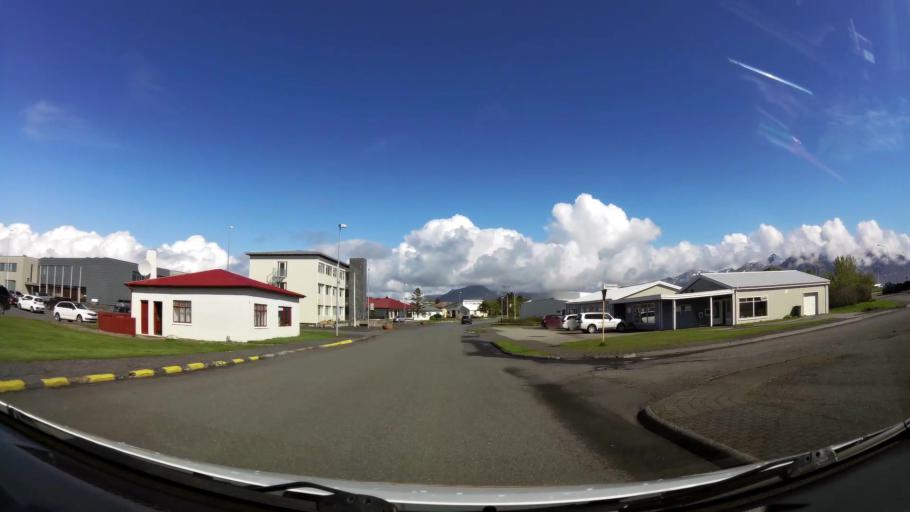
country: IS
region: East
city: Hoefn
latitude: 64.2525
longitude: -15.2109
